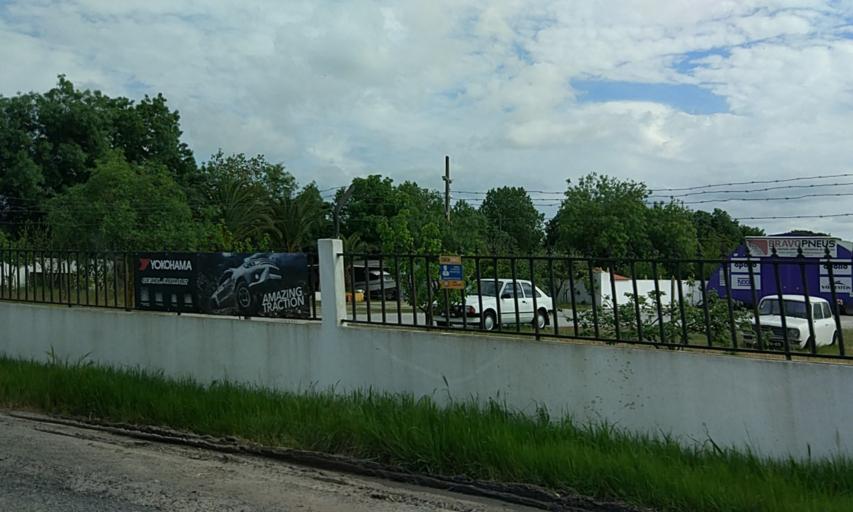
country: PT
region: Evora
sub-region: Evora
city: Evora
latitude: 38.5676
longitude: -7.9482
